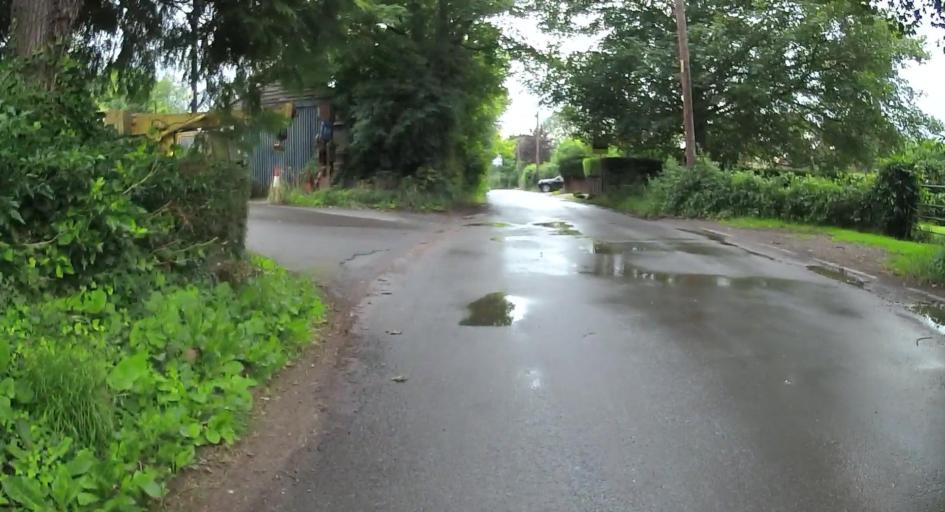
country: GB
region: England
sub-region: Hampshire
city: Andover
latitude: 51.2181
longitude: -1.4408
